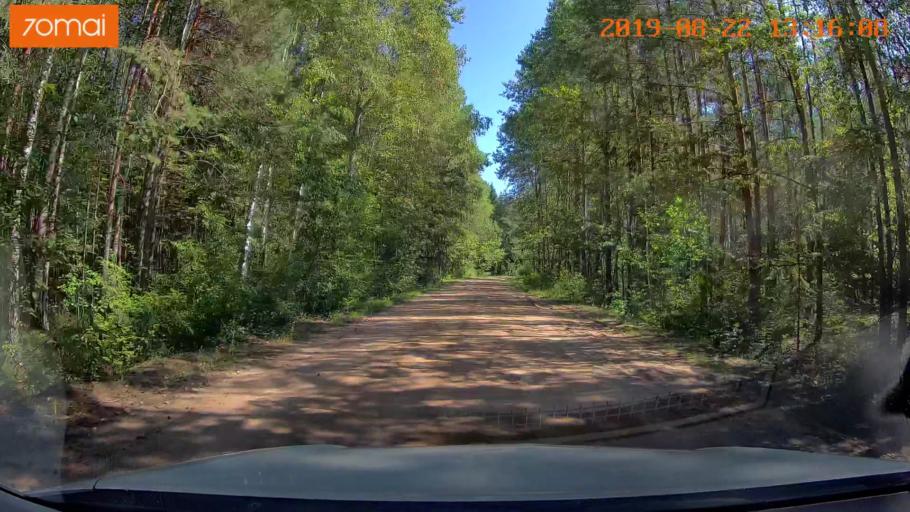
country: BY
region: Minsk
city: Prawdzinski
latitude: 53.2571
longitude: 27.9076
